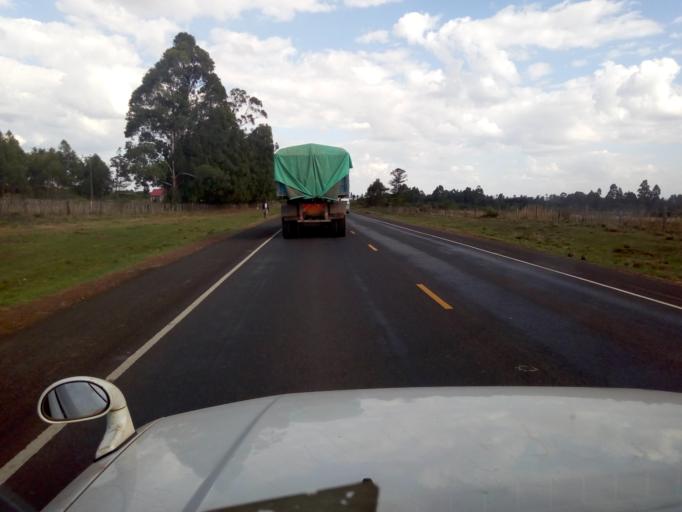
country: KE
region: Uasin Gishu
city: Eldoret
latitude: 0.3493
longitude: 35.3610
